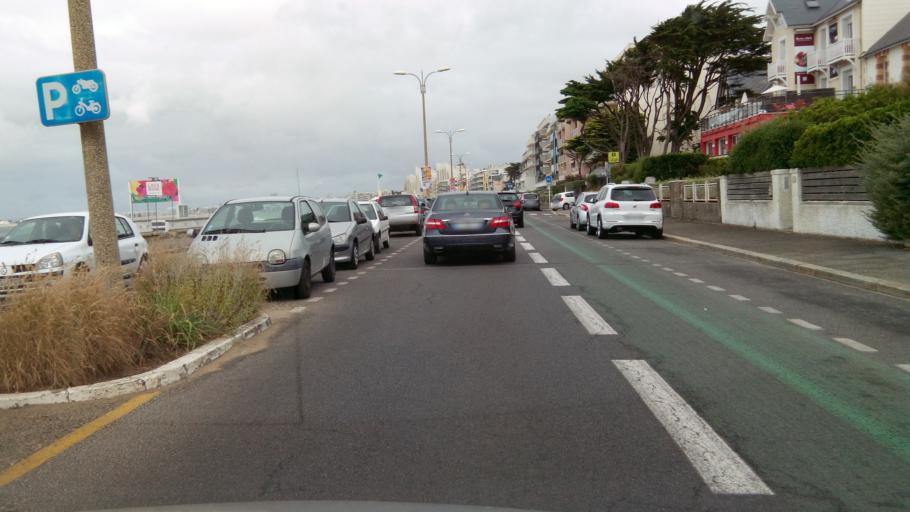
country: FR
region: Pays de la Loire
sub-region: Departement de la Loire-Atlantique
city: Pornichet
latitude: 47.2692
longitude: -2.3502
